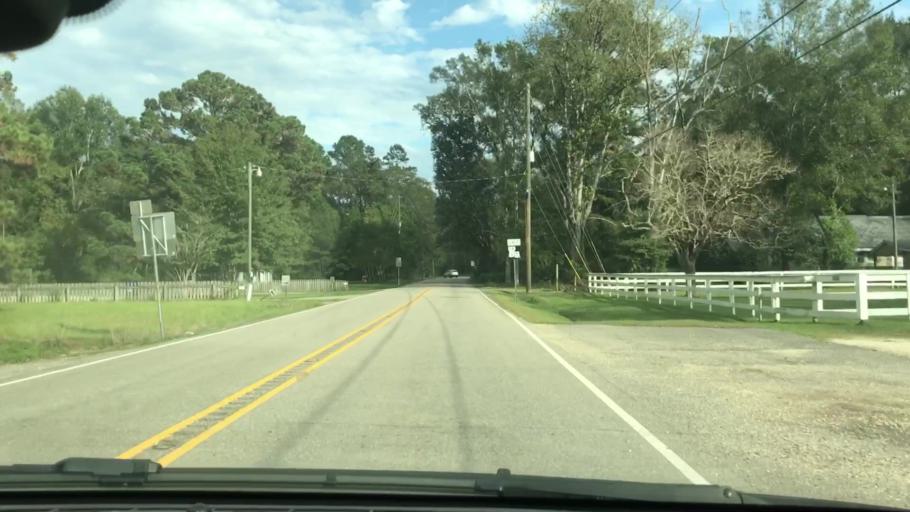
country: US
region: Louisiana
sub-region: Saint Tammany Parish
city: Abita Springs
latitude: 30.5326
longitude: -89.8752
